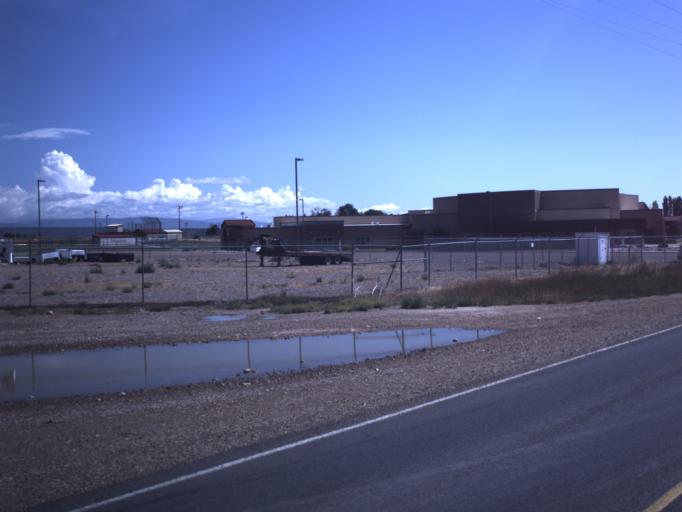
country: US
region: Utah
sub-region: Duchesne County
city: Duchesne
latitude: 40.3592
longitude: -110.2939
